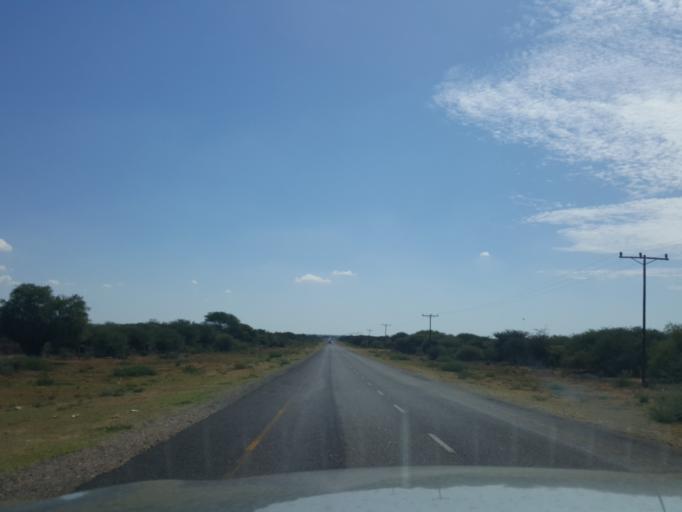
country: BW
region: Kweneng
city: Letlhakeng
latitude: -24.1205
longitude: 25.0746
